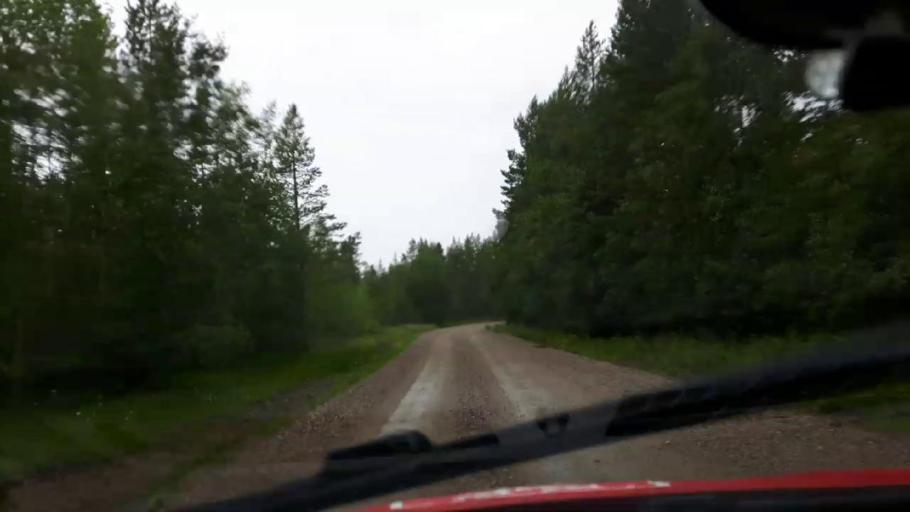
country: SE
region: Jaemtland
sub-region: OEstersunds Kommun
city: Brunflo
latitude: 62.8099
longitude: 14.8897
